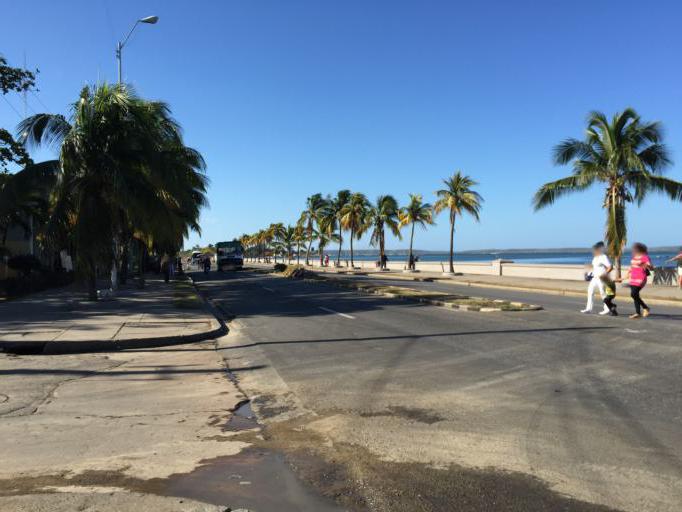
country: CU
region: Cienfuegos
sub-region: Municipio de Cienfuegos
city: Cienfuegos
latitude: 22.1382
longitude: -80.4490
